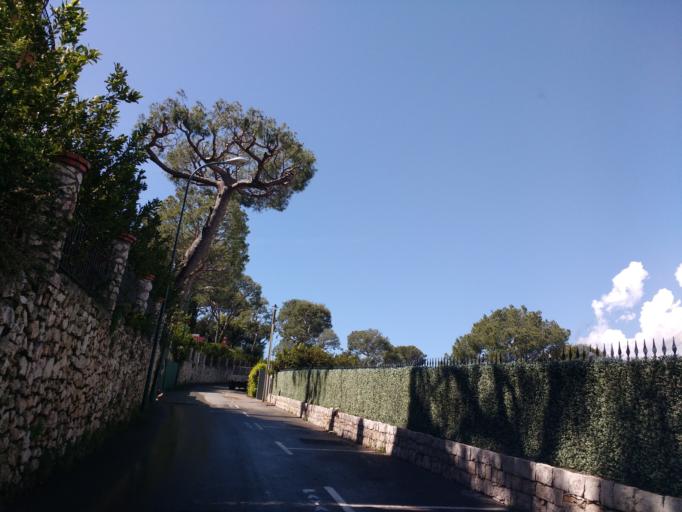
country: FR
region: Provence-Alpes-Cote d'Azur
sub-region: Departement des Alpes-Maritimes
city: Saint-Jean-Cap-Ferrat
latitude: 43.6918
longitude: 7.3225
